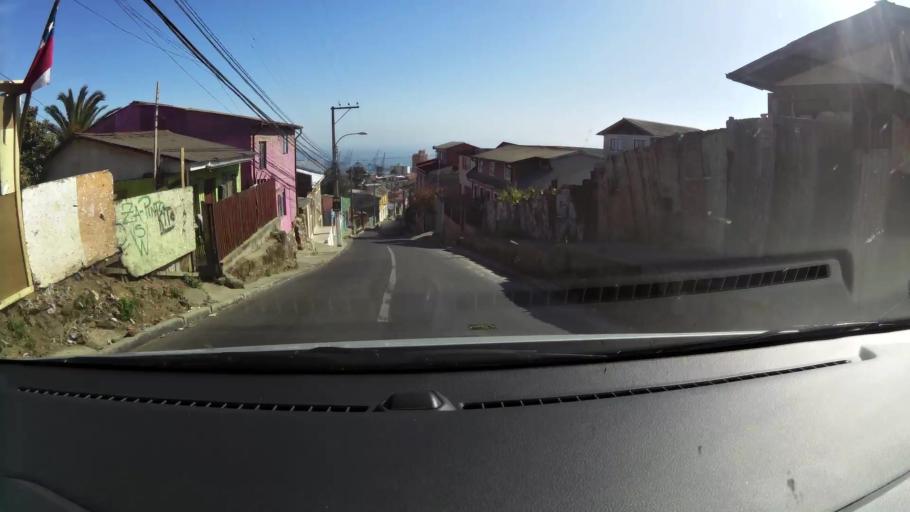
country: CL
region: Valparaiso
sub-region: Provincia de Valparaiso
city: Valparaiso
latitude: -33.0487
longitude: -71.6350
